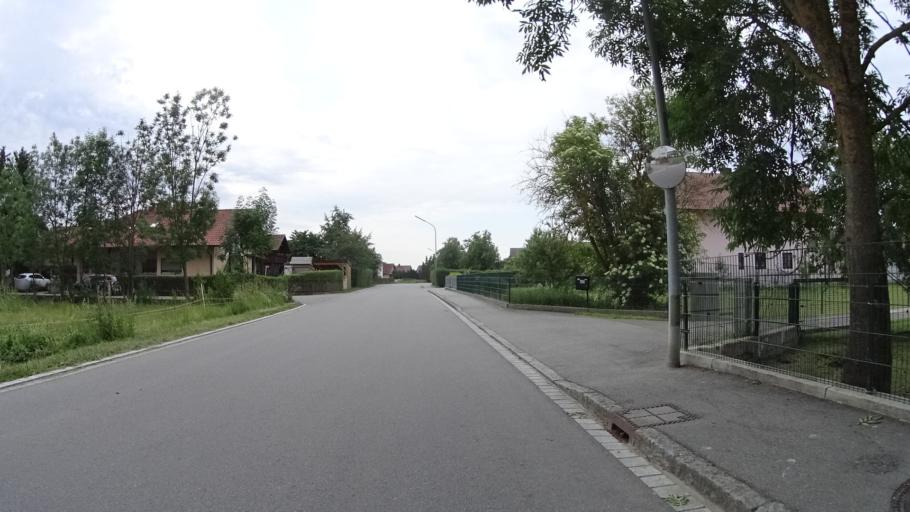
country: DE
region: Bavaria
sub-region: Lower Bavaria
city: Kirchroth
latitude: 48.9271
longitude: 12.5528
